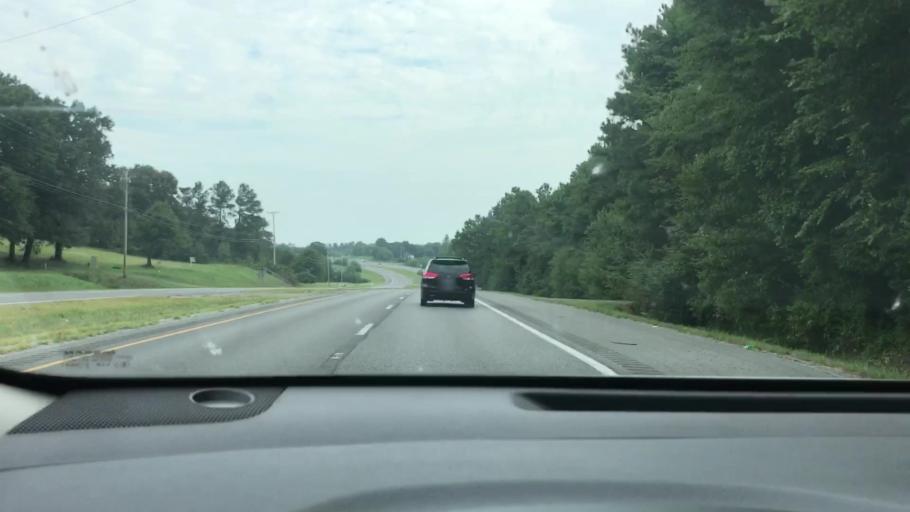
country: US
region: Kentucky
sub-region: Calloway County
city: Murray
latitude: 36.6696
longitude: -88.3036
